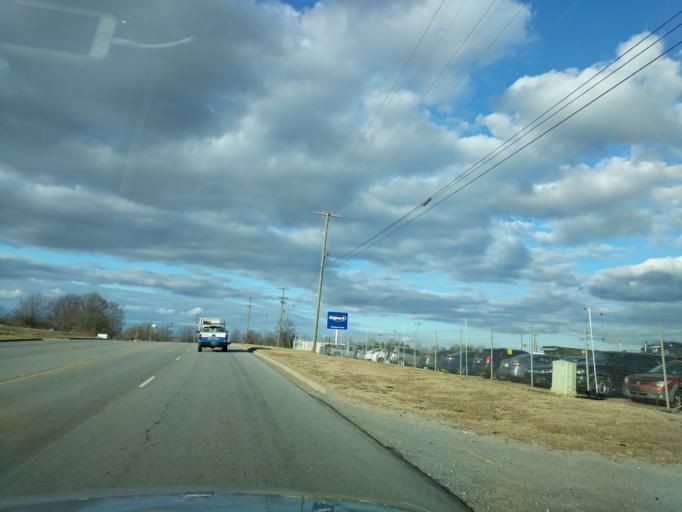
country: US
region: South Carolina
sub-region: Spartanburg County
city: Duncan
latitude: 34.8661
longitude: -82.1418
